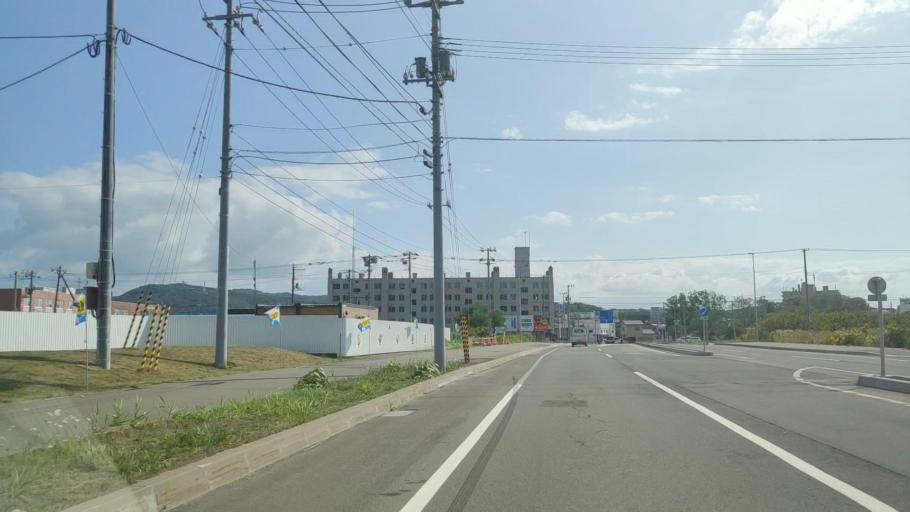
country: JP
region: Hokkaido
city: Rumoi
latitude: 43.9438
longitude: 141.6476
